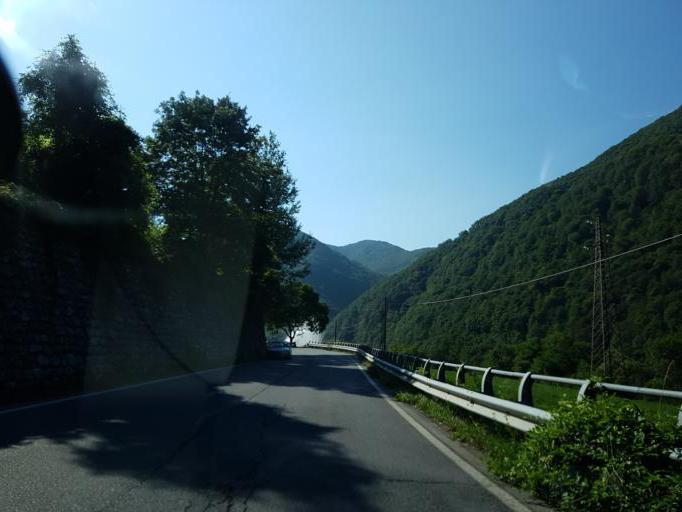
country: IT
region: Piedmont
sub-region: Provincia di Cuneo
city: San Damiano Macra
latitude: 44.4892
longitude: 7.2455
